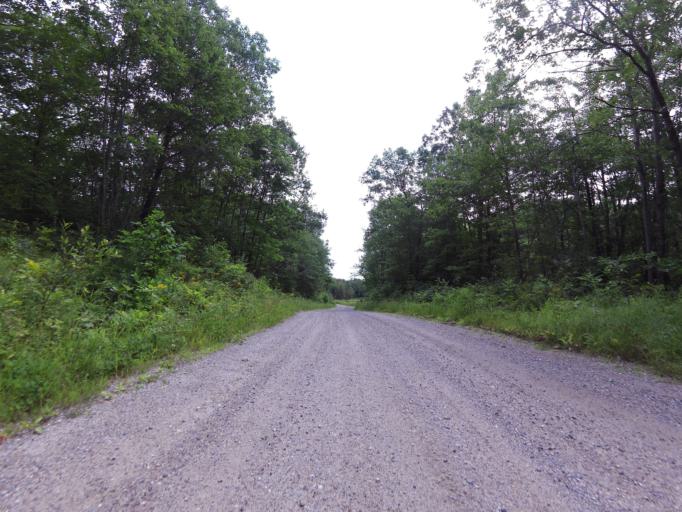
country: CA
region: Ontario
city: Perth
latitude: 44.7532
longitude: -76.6155
